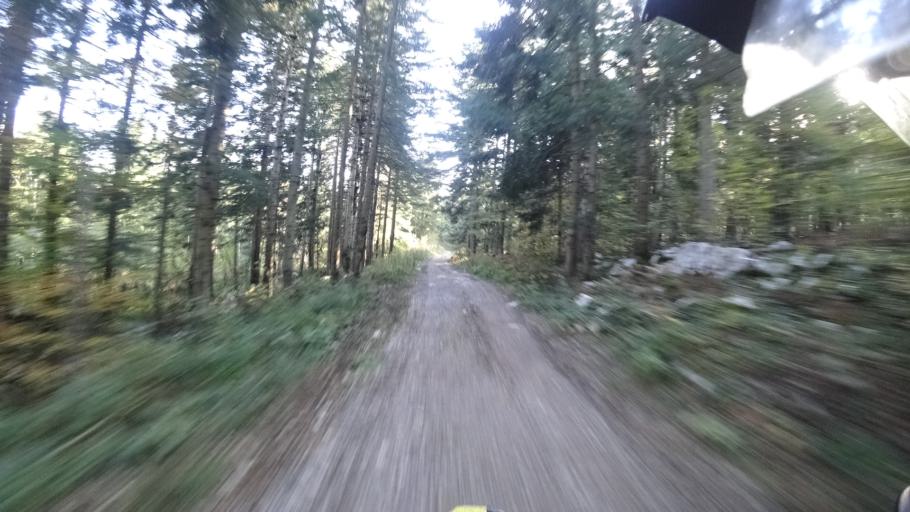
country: HR
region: Karlovacka
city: Plaski
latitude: 45.0114
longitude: 15.4019
